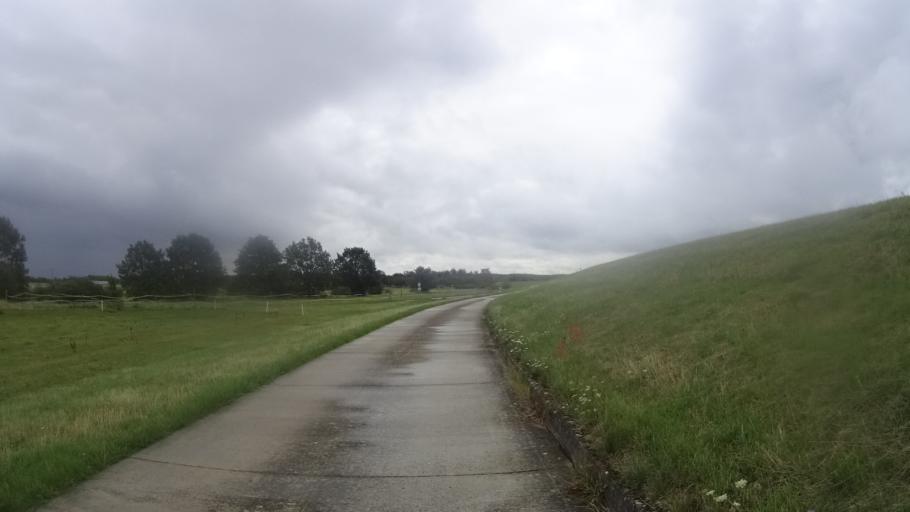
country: DE
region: Lower Saxony
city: Neu Darchau
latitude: 53.2548
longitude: 10.8635
